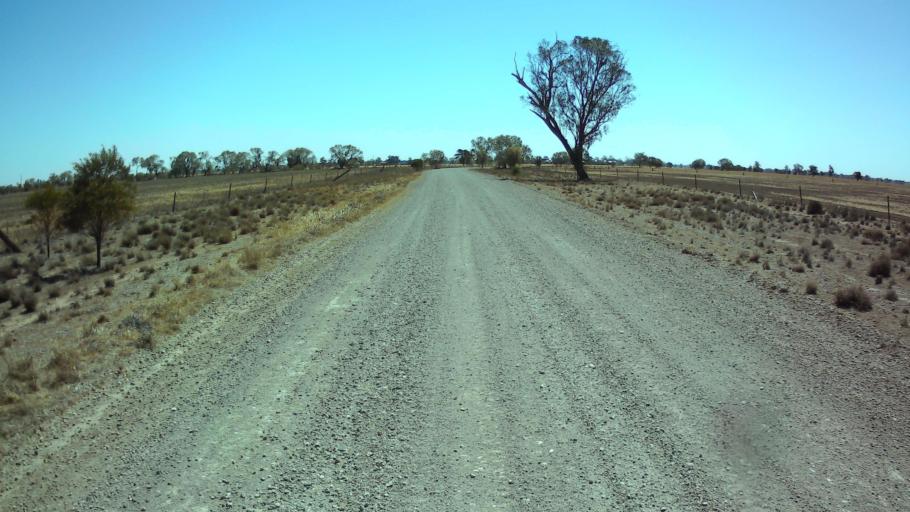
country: AU
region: New South Wales
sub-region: Forbes
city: Forbes
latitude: -33.7466
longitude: 147.7281
